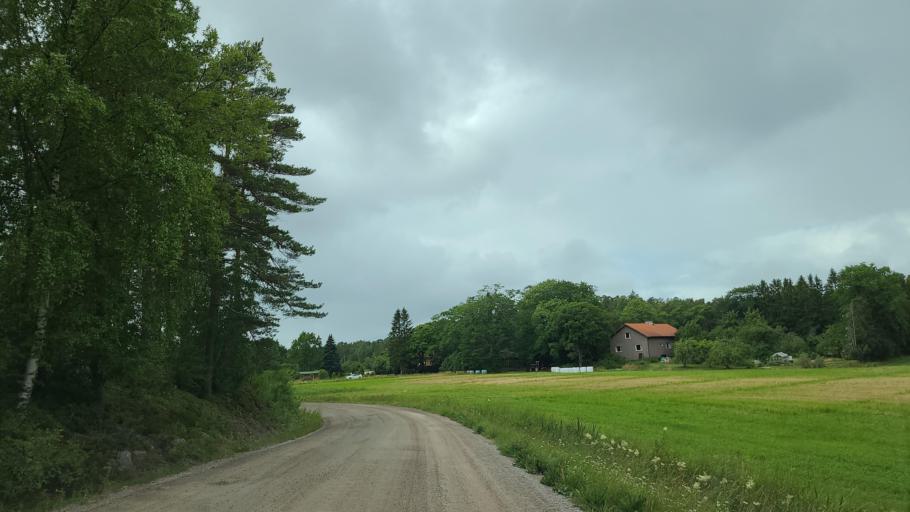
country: FI
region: Varsinais-Suomi
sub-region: Aboland-Turunmaa
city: Nagu
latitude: 60.2015
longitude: 21.8843
